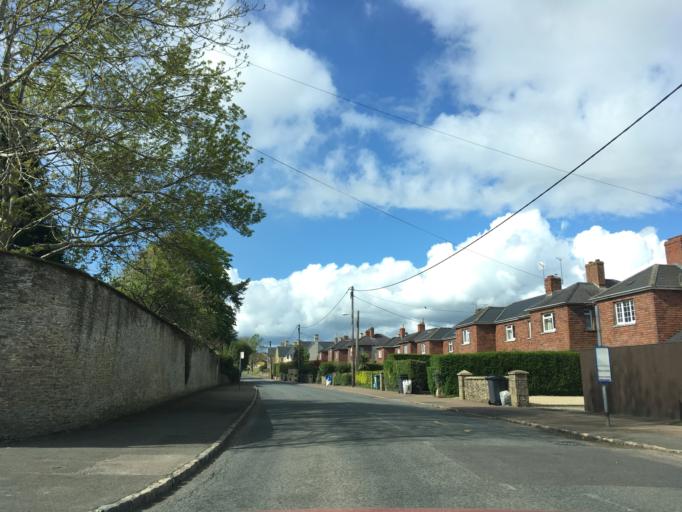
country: GB
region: England
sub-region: Gloucestershire
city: Tetbury
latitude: 51.6412
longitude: -2.1634
